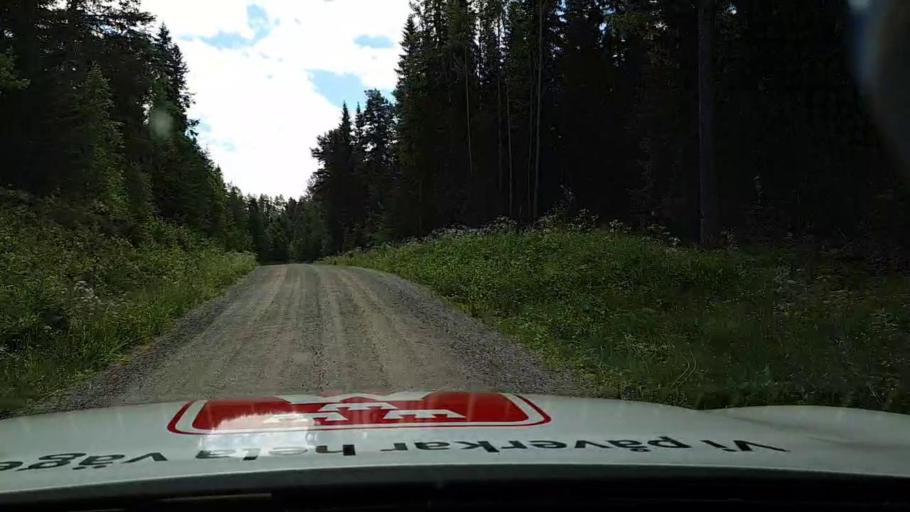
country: SE
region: Jaemtland
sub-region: Braecke Kommun
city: Braecke
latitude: 62.7579
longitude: 15.5009
